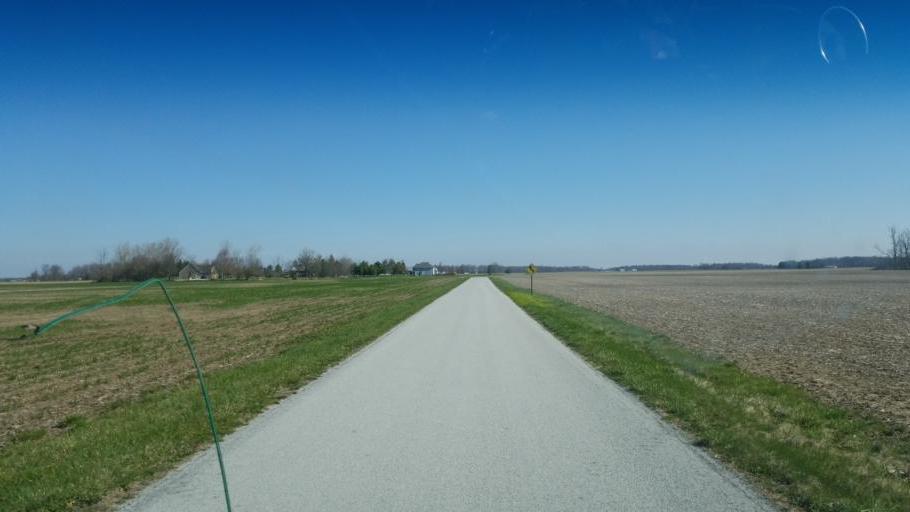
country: US
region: Ohio
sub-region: Hardin County
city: Kenton
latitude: 40.6917
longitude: -83.5592
